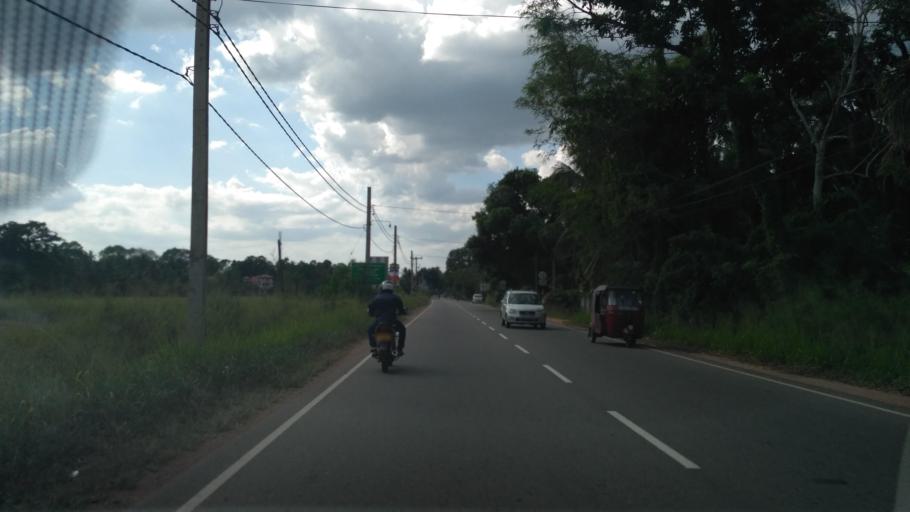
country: LK
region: North Western
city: Kuliyapitiya
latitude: 7.3263
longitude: 80.0312
